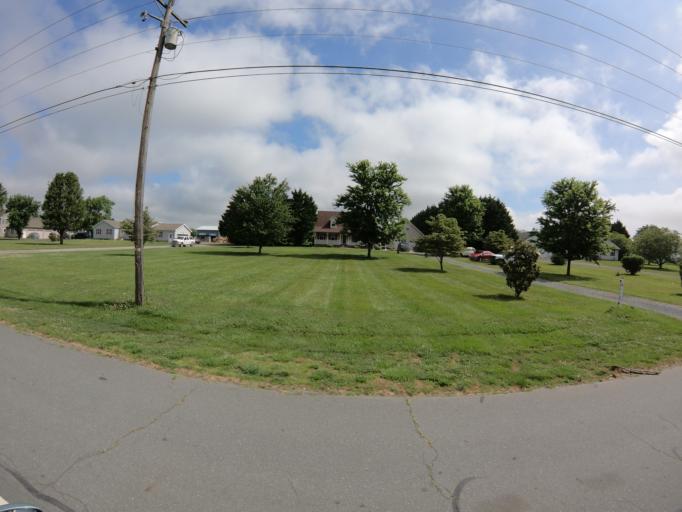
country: US
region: Delaware
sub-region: Kent County
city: Riverview
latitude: 39.0101
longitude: -75.4842
